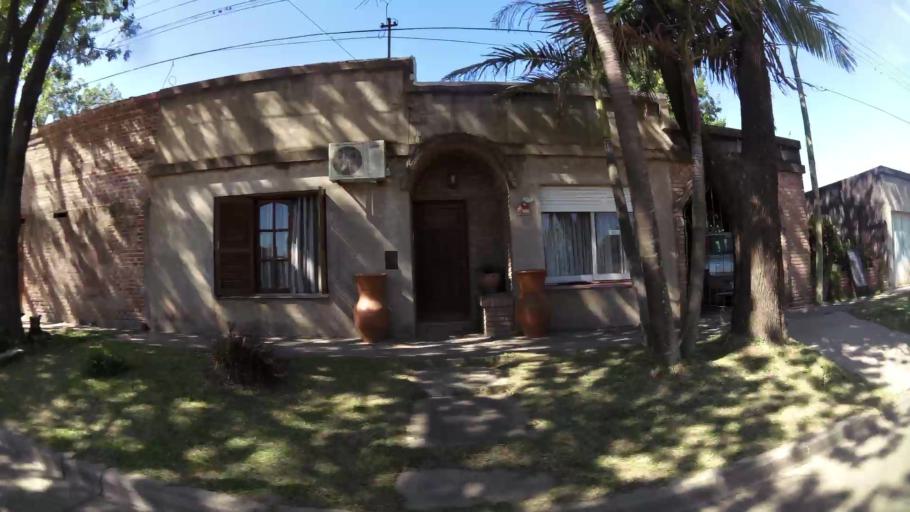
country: AR
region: Santa Fe
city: Esperanza
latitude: -31.4632
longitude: -60.9351
